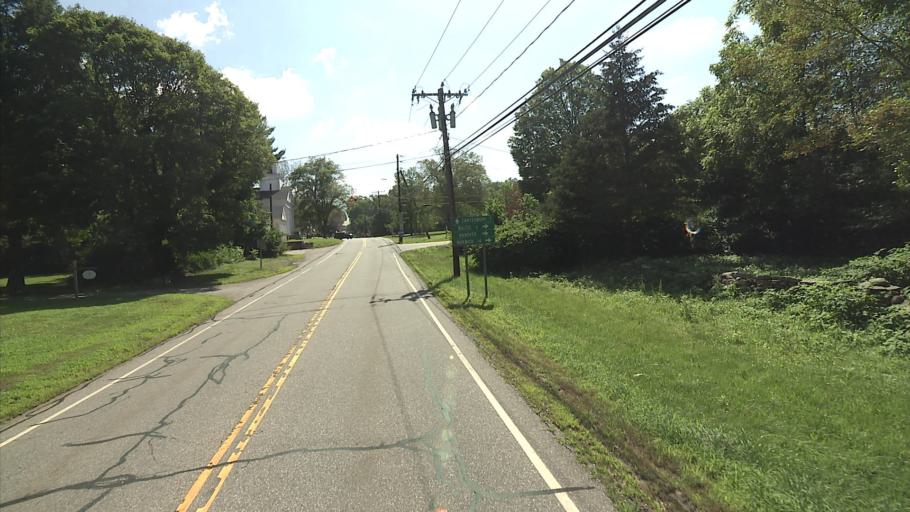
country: US
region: Connecticut
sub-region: Windham County
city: Windham
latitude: 41.6985
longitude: -72.0832
